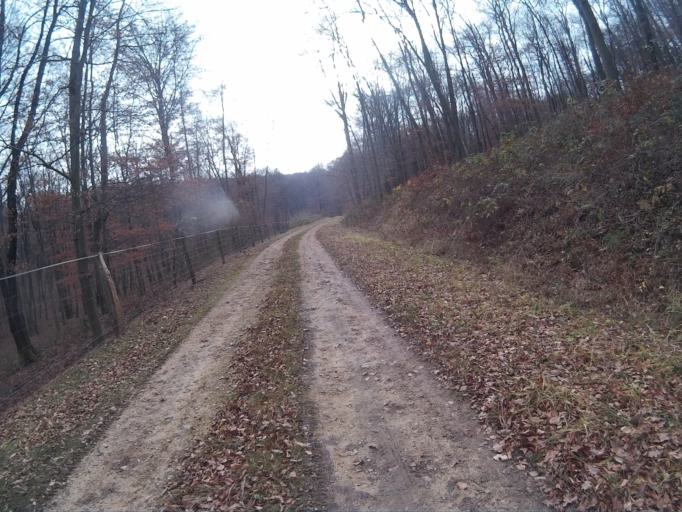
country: HU
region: Veszprem
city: Tapolca
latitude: 46.9806
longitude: 17.5021
